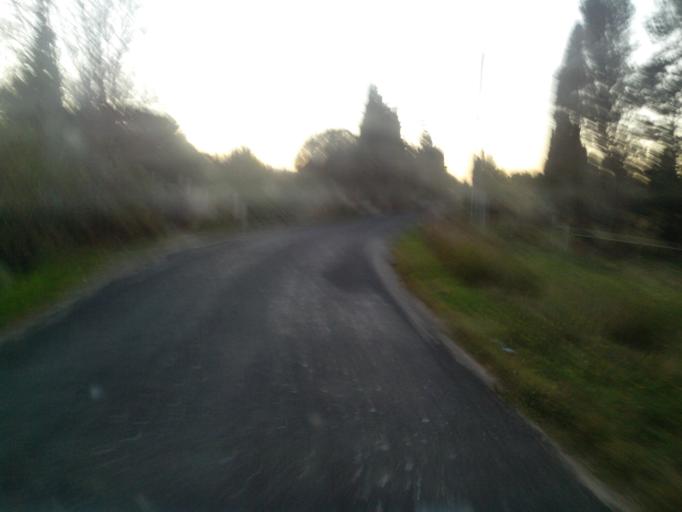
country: FR
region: Languedoc-Roussillon
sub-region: Departement des Pyrenees-Orientales
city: Rivesaltes
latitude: 42.7715
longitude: 2.8559
